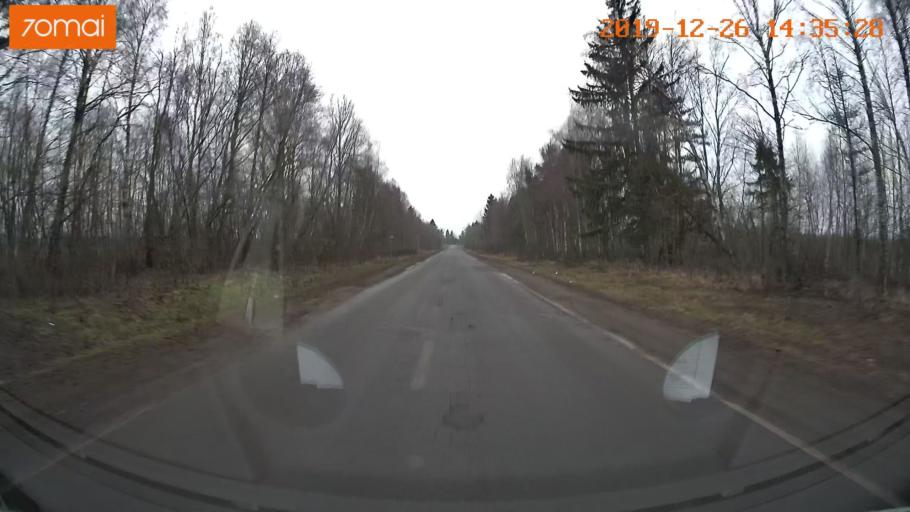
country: RU
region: Jaroslavl
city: Poshekhon'ye
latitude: 58.4201
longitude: 38.9843
